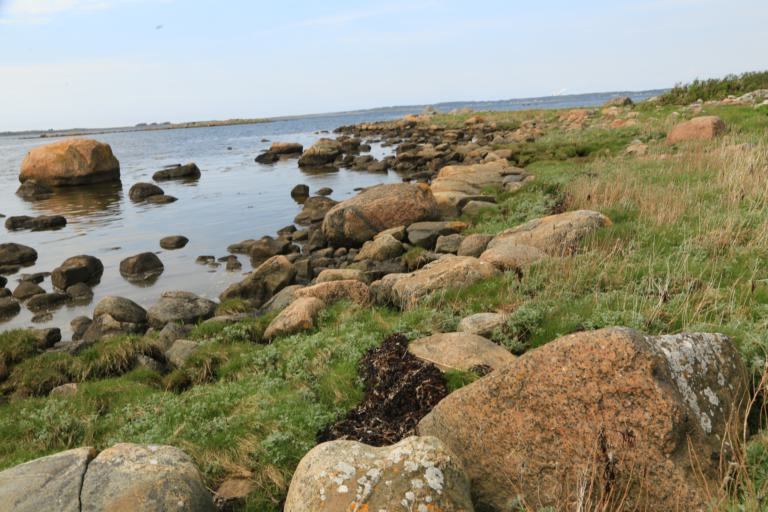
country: SE
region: Halland
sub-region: Varbergs Kommun
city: Varberg
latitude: 57.1481
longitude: 12.2066
